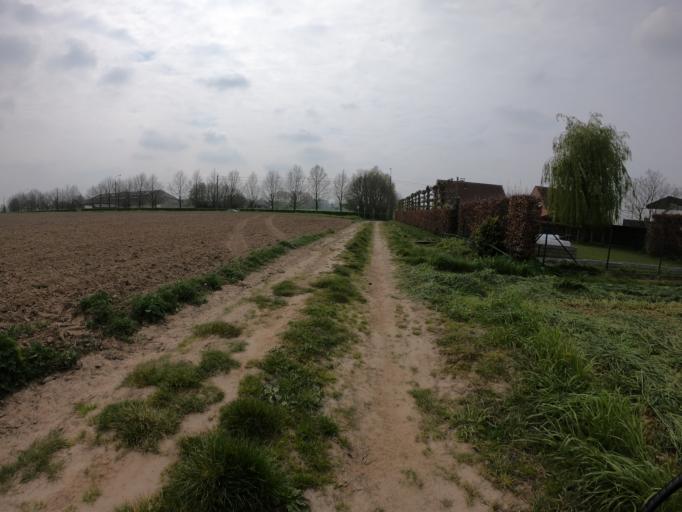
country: BE
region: Wallonia
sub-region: Province du Hainaut
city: Celles
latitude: 50.7475
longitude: 3.4856
